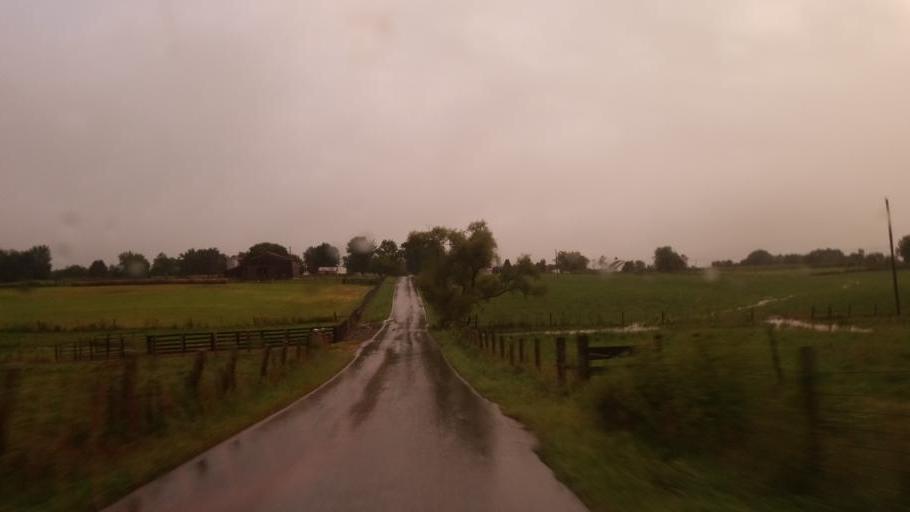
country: US
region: Kentucky
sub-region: Fleming County
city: Flemingsburg
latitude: 38.4505
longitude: -83.6422
